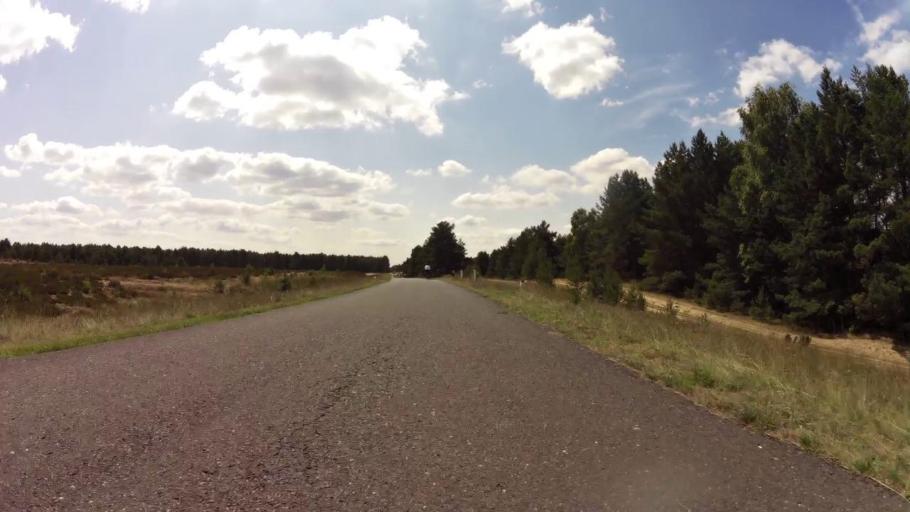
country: PL
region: West Pomeranian Voivodeship
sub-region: Powiat drawski
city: Drawsko Pomorskie
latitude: 53.4112
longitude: 15.7368
